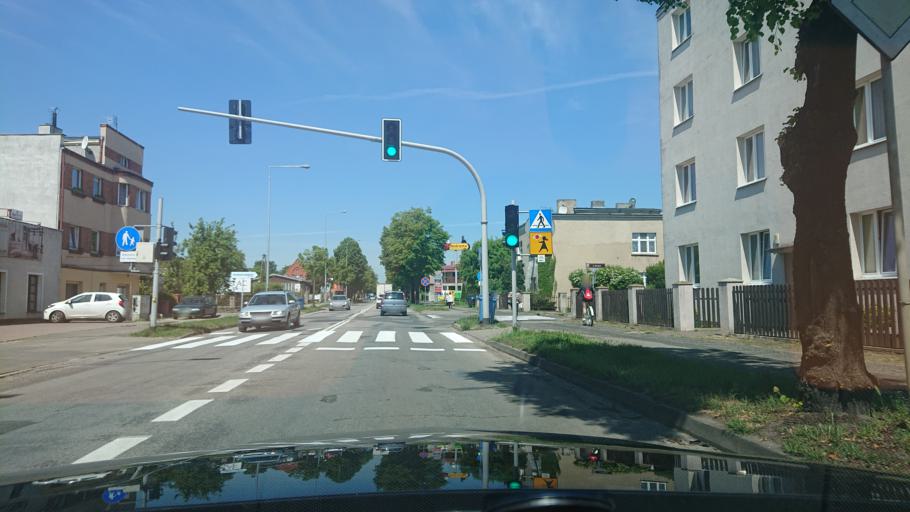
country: PL
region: Greater Poland Voivodeship
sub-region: Powiat gnieznienski
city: Gniezno
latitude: 52.5241
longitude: 17.6012
